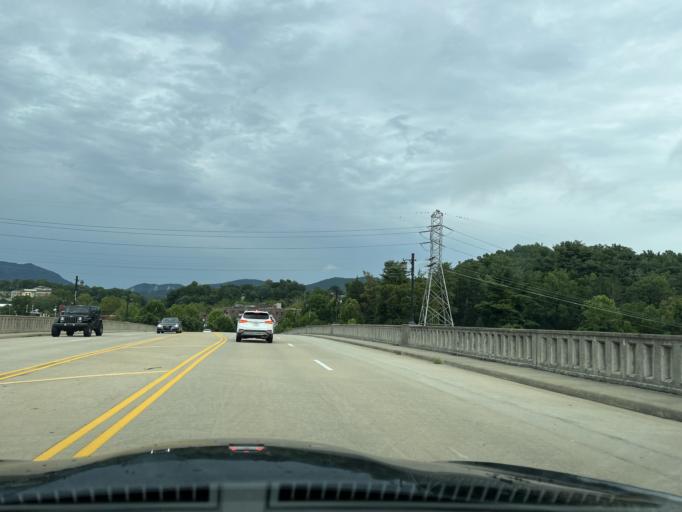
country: US
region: North Carolina
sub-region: Buncombe County
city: Asheville
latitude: 35.5684
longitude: -82.5470
